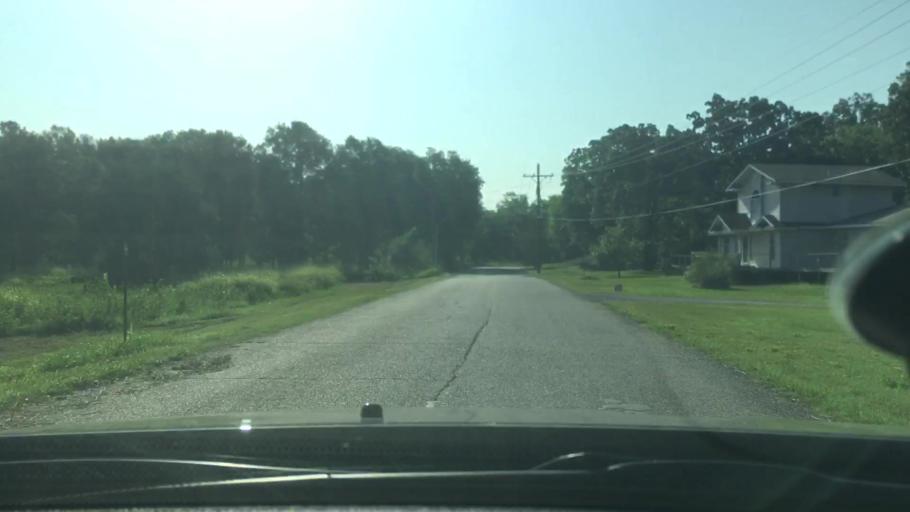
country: US
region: Oklahoma
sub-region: Atoka County
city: Atoka
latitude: 34.3899
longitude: -96.1316
